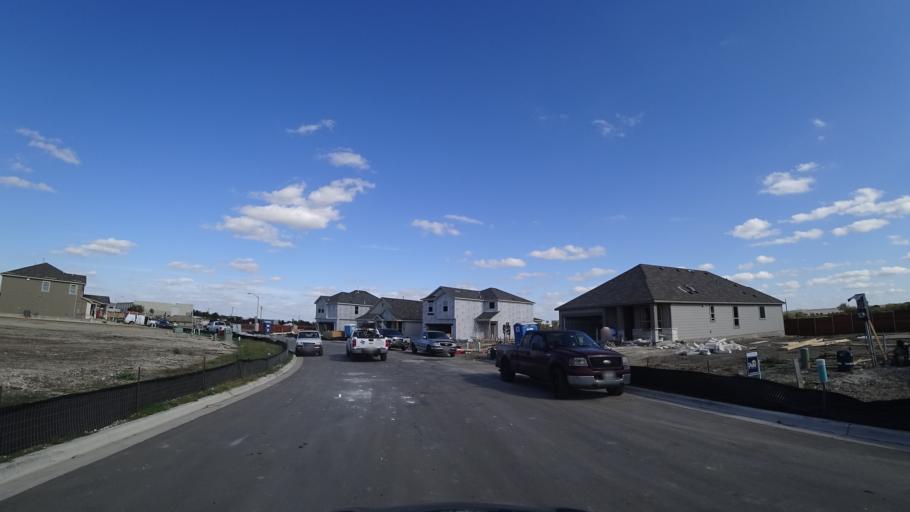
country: US
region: Texas
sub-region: Travis County
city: Wells Branch
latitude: 30.4650
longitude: -97.6797
